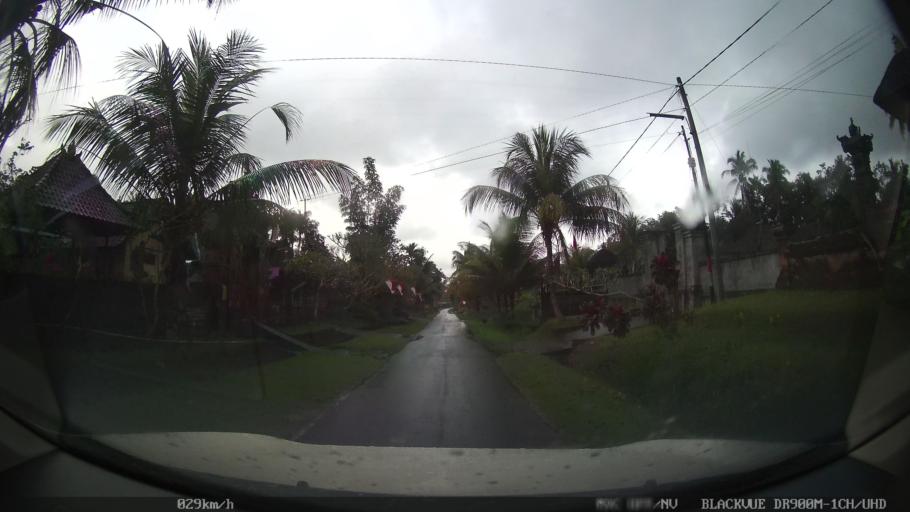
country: ID
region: Bali
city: Banjar Tengah
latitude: -8.4922
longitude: 115.1883
